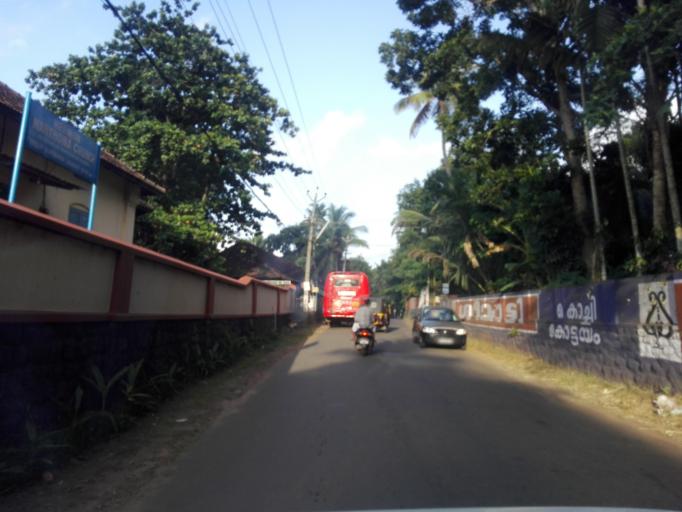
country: IN
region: Kerala
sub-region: Kottayam
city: Kottayam
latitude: 9.6118
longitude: 76.4997
